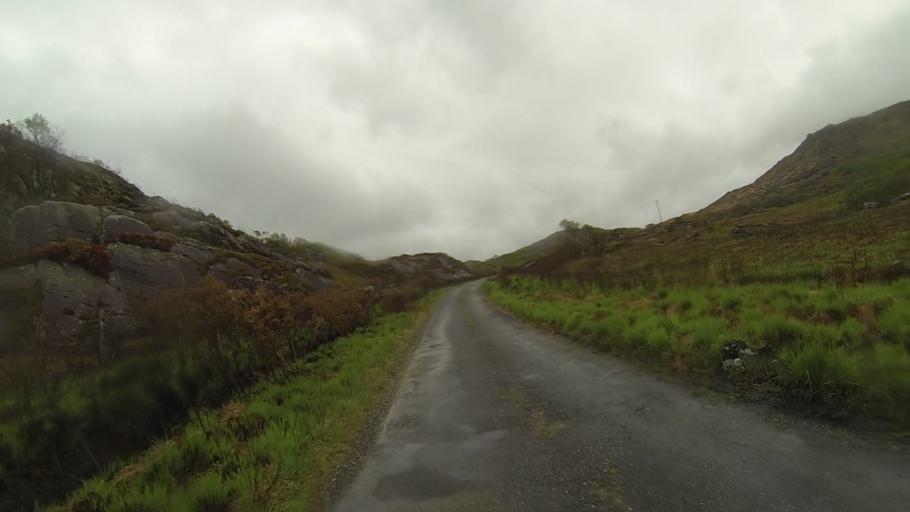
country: IE
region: Munster
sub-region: Ciarrai
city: Kenmare
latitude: 51.9699
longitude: -9.6362
